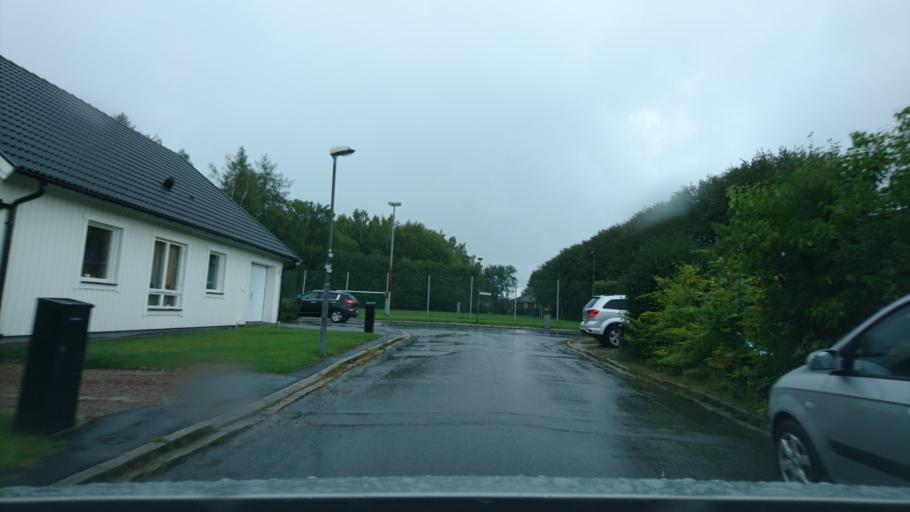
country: SE
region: Uppsala
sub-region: Uppsala Kommun
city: Gamla Uppsala
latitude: 59.8798
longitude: 17.6138
